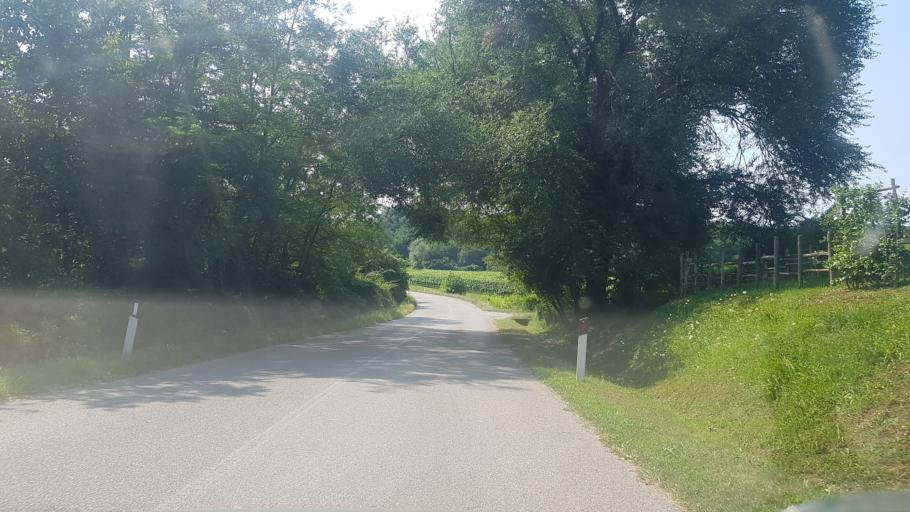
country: IT
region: Friuli Venezia Giulia
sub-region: Provincia di Gorizia
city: Mossa
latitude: 45.9563
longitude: 13.5654
